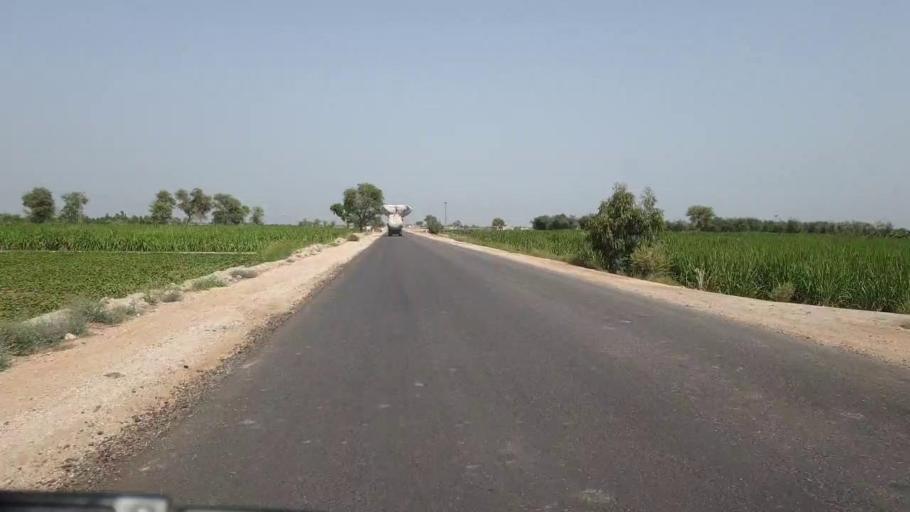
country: PK
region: Sindh
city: Sakrand
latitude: 26.2686
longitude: 68.1667
